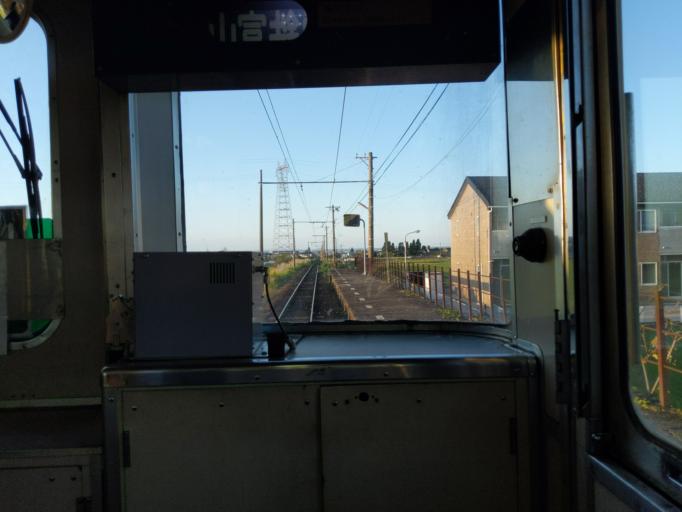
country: JP
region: Toyama
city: Kamiichi
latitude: 36.6479
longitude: 137.3179
